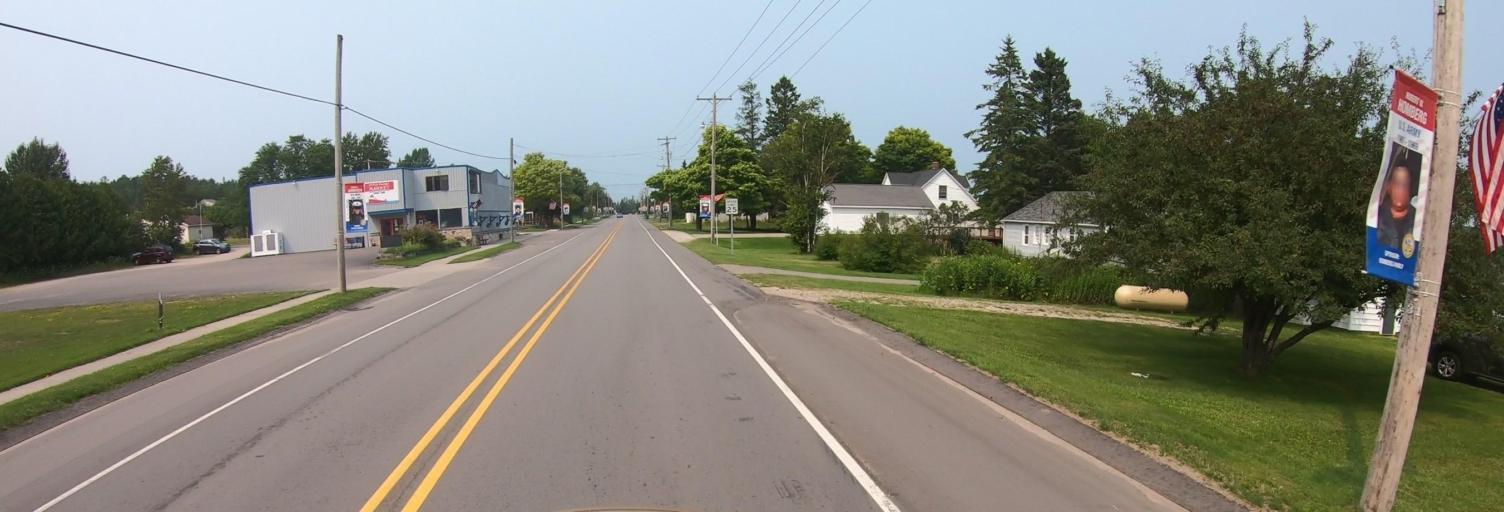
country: CA
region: Ontario
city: Thessalon
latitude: 45.9952
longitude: -83.9017
